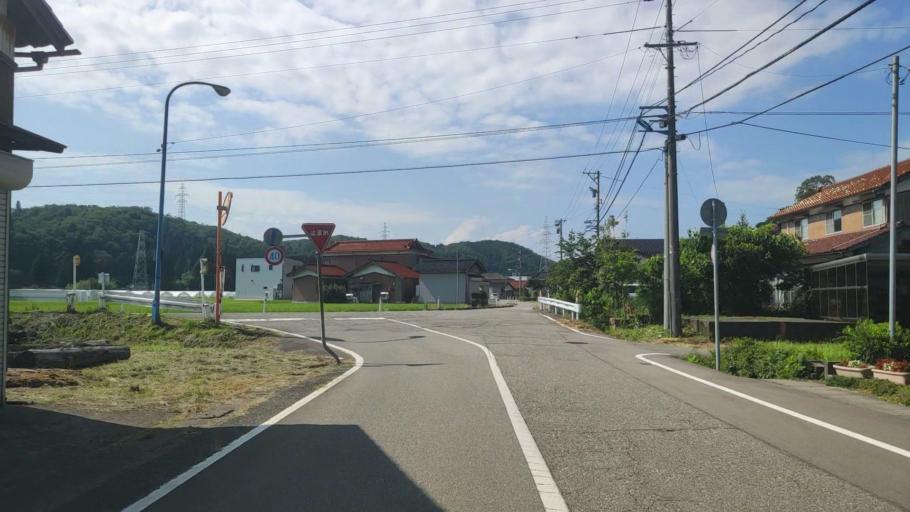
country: JP
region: Ishikawa
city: Komatsu
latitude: 36.3723
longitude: 136.4980
